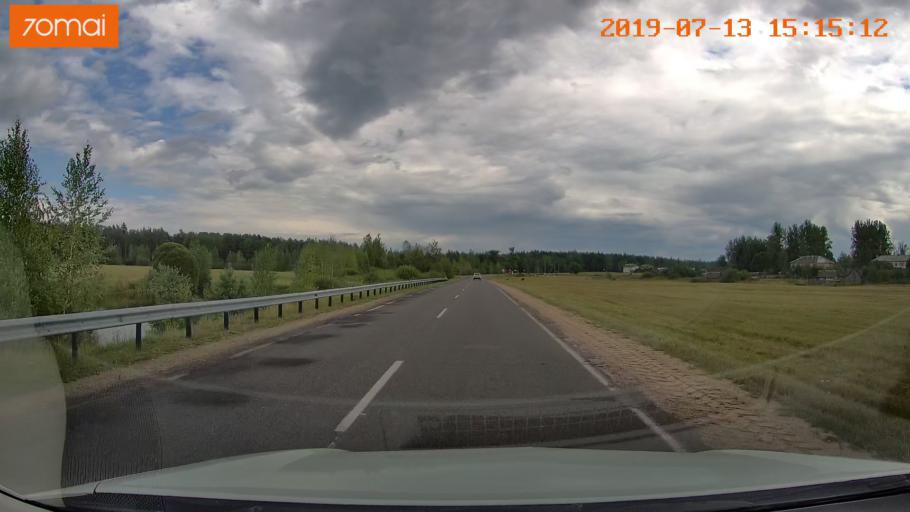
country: BY
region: Mogilev
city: Hlusha
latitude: 53.1186
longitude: 28.8235
